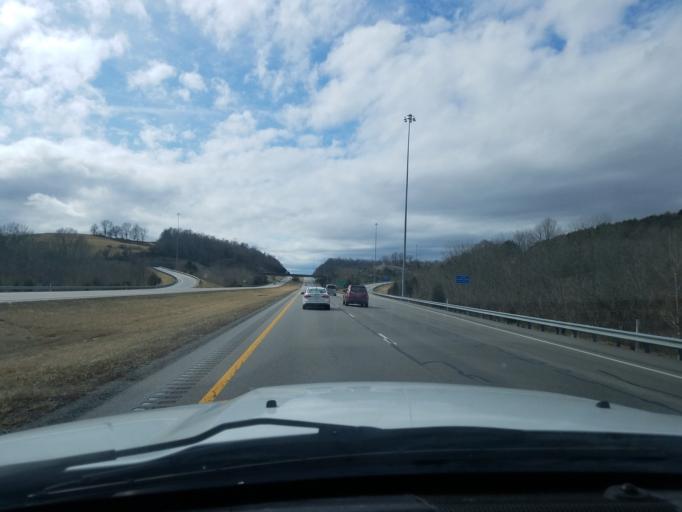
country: US
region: Kentucky
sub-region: Bath County
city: Owingsville
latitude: 38.1294
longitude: -83.7463
